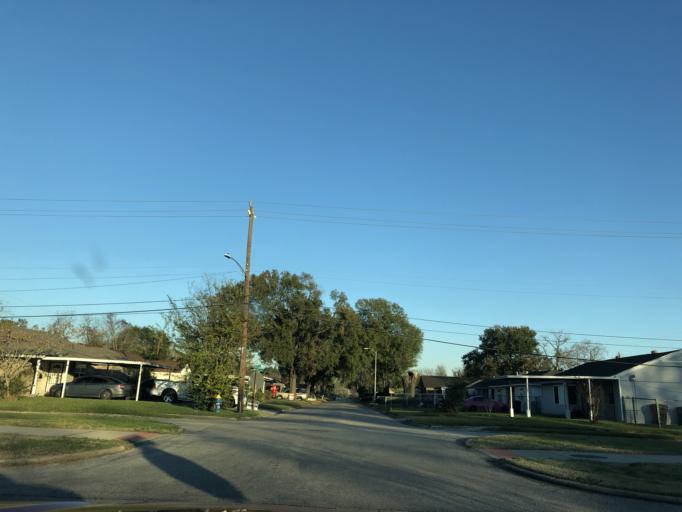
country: US
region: Texas
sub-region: Harris County
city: Jacinto City
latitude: 29.7610
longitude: -95.2701
